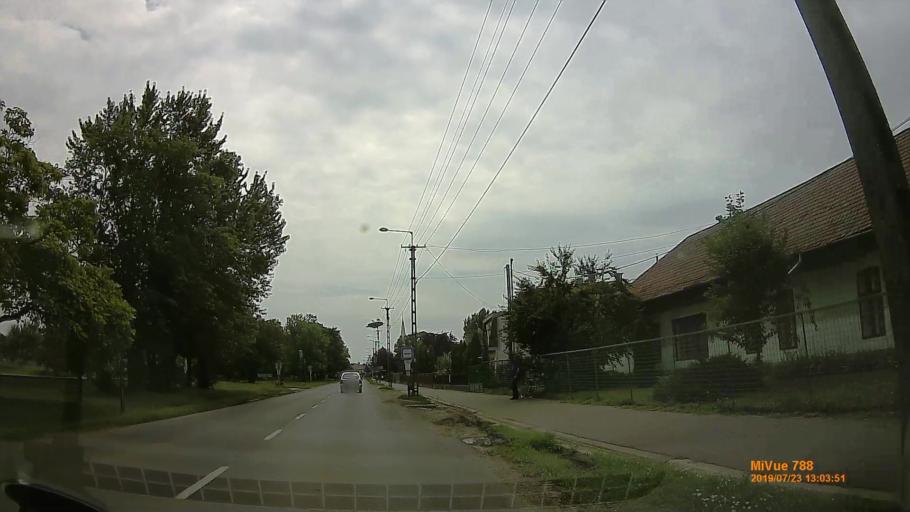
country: HU
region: Szabolcs-Szatmar-Bereg
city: Tiszavasvari
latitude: 47.9547
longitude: 21.3693
